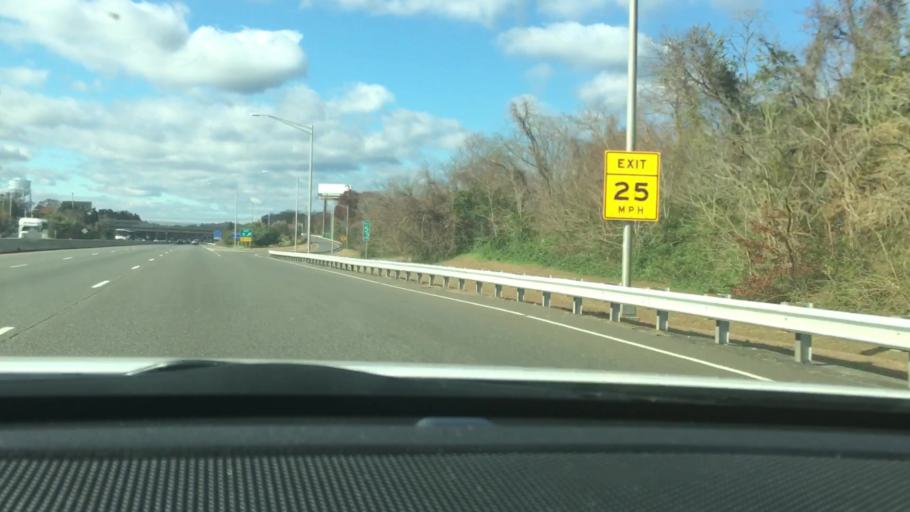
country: US
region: New Jersey
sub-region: Atlantic County
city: Pleasantville
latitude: 39.4002
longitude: -74.5202
